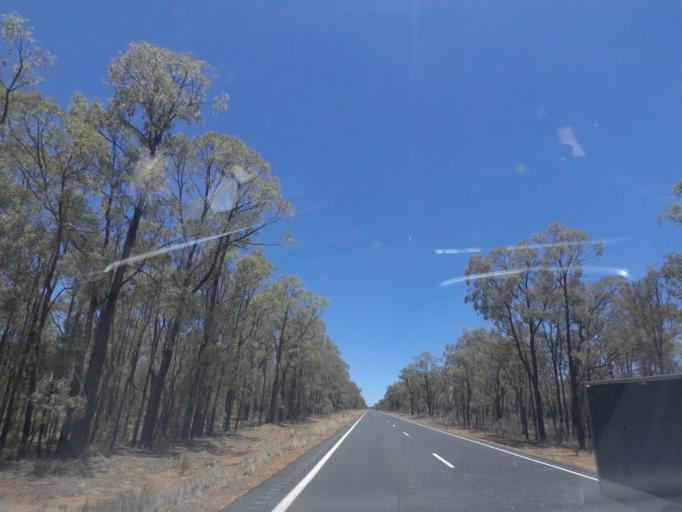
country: AU
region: New South Wales
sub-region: Warrumbungle Shire
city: Coonabarabran
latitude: -30.8602
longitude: 149.4544
